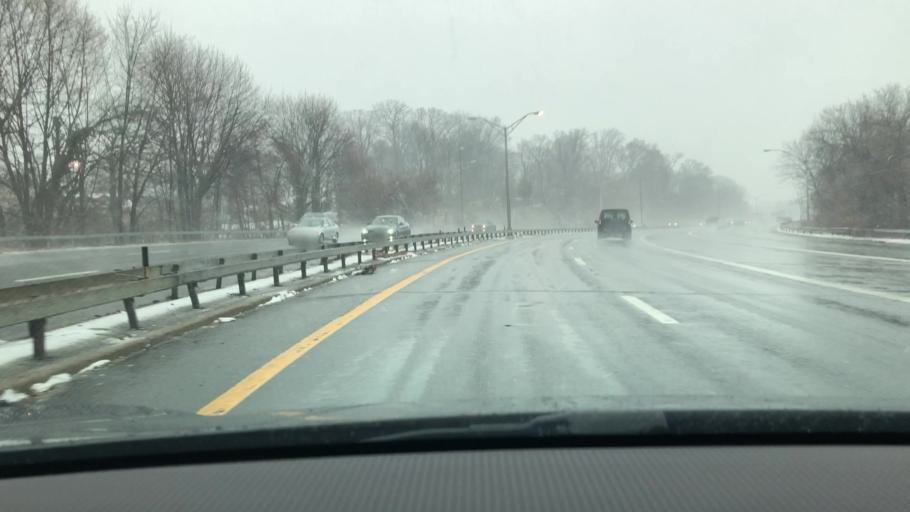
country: US
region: New York
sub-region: Westchester County
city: Bronxville
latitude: 40.9356
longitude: -73.8076
